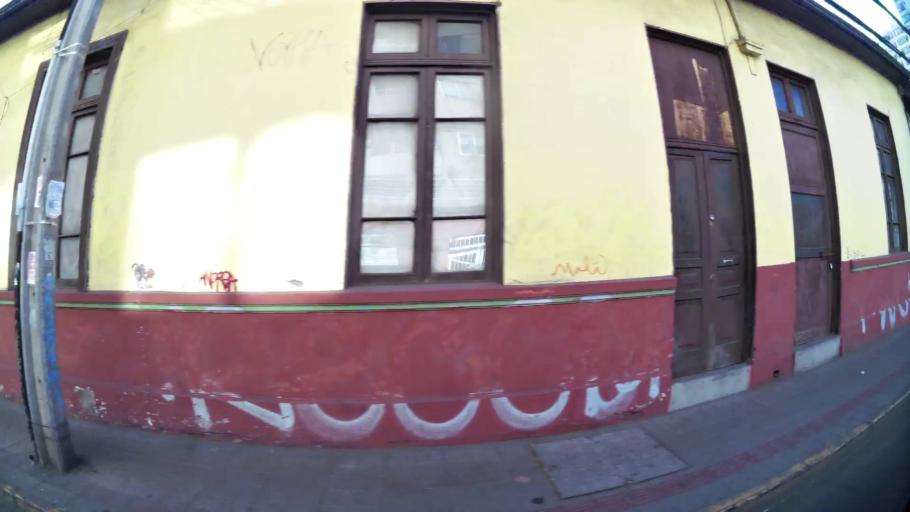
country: CL
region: Santiago Metropolitan
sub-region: Provincia de Santiago
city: Santiago
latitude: -33.4304
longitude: -70.6421
